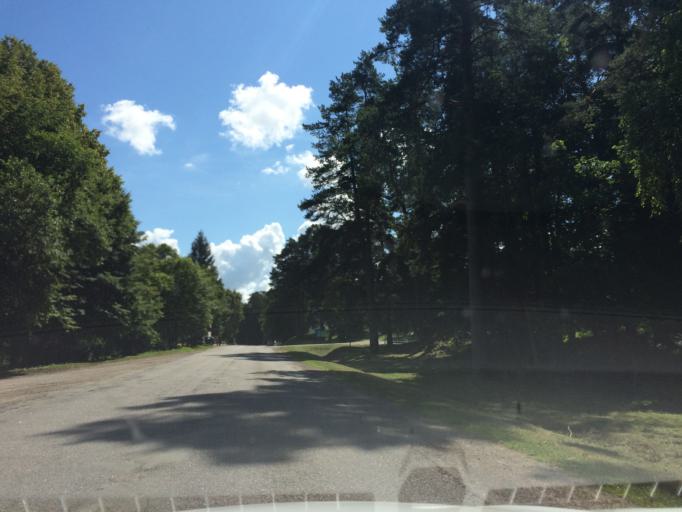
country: LV
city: Tervete
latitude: 56.4815
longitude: 23.3786
